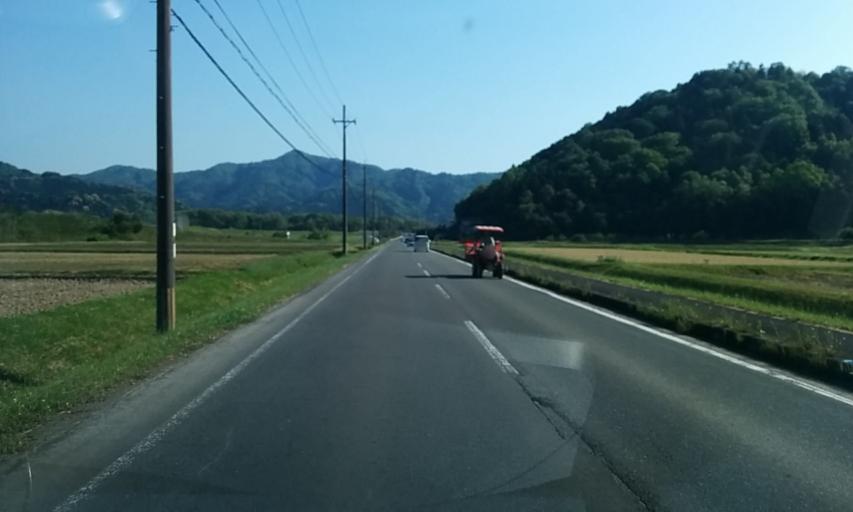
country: JP
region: Kyoto
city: Ayabe
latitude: 35.3160
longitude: 135.2093
